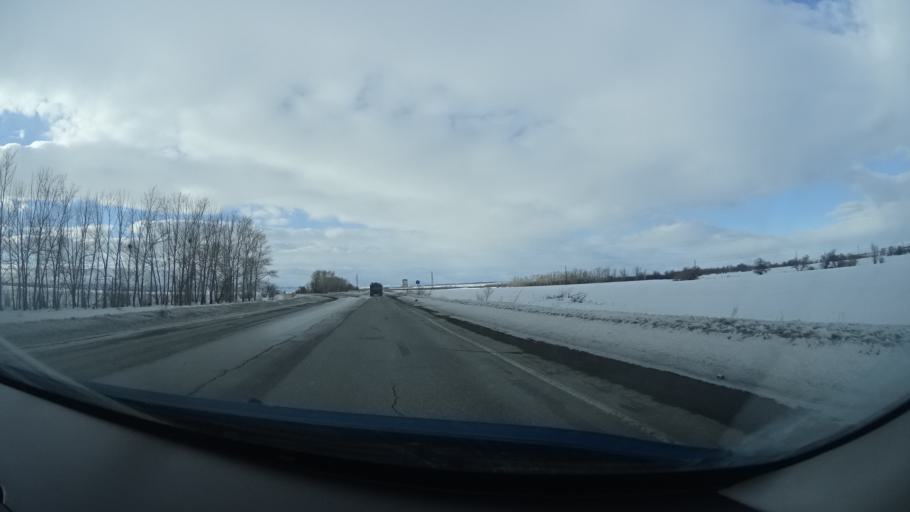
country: RU
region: Chelyabinsk
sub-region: Gorod Magnitogorsk
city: Magnitogorsk
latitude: 53.5813
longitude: 58.8865
